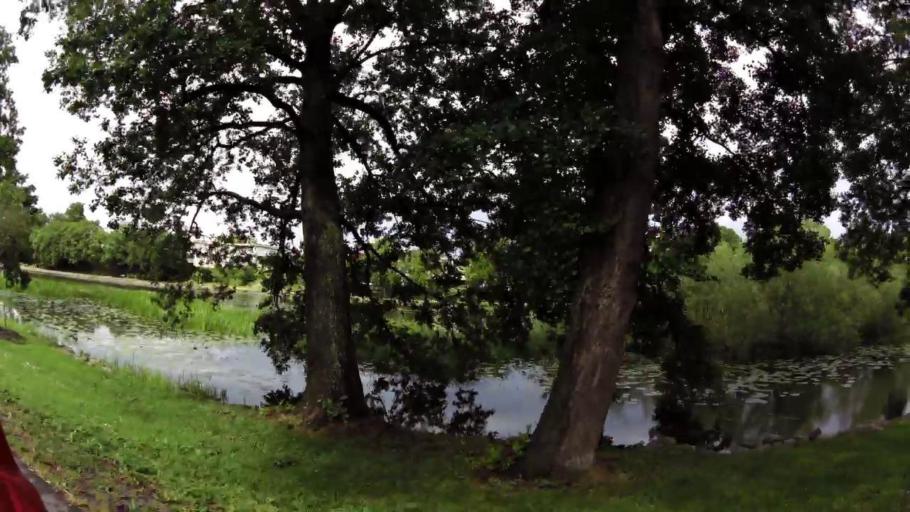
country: SE
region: OEstergoetland
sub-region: Linkopings Kommun
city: Linkoping
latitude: 58.4016
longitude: 15.6443
